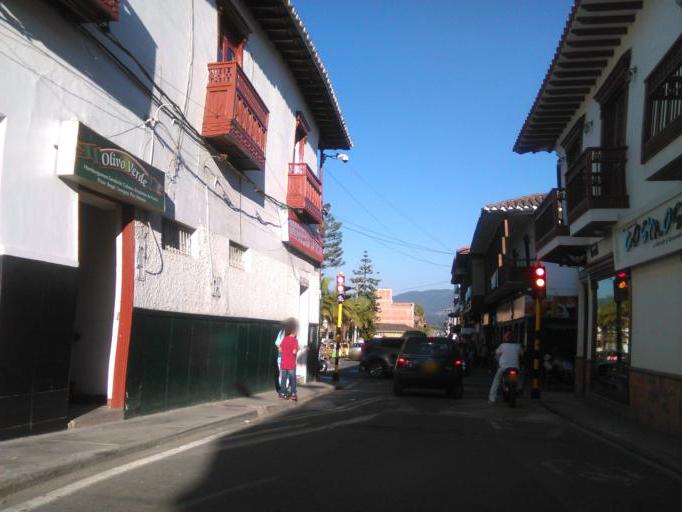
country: CO
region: Antioquia
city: La Ceja
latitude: 6.0305
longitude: -75.4325
